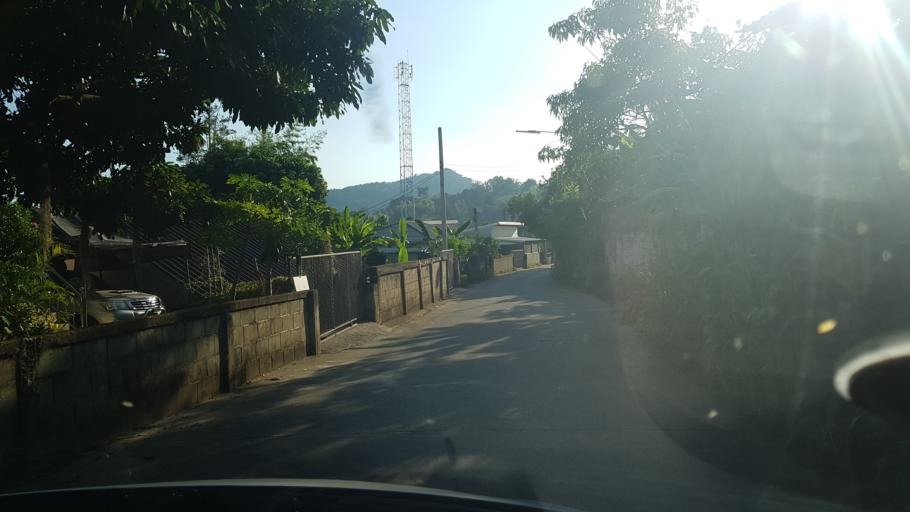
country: TH
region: Chiang Rai
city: Chiang Rai
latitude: 19.9460
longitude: 99.8063
